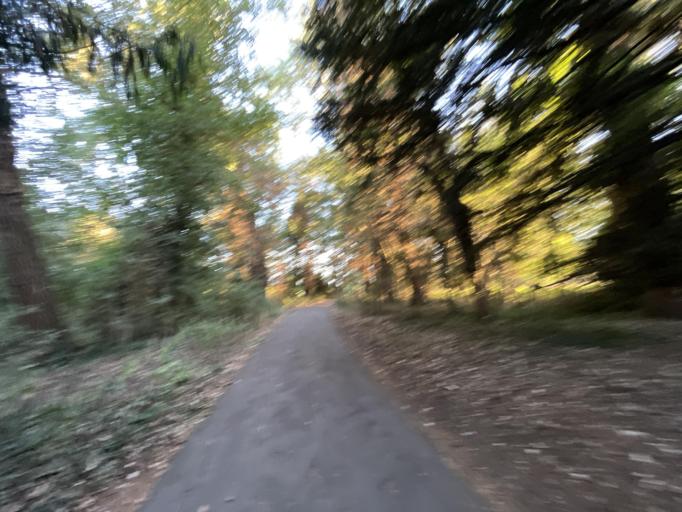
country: GB
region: England
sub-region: Surrey
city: East Horsley
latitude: 51.2669
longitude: -0.4248
